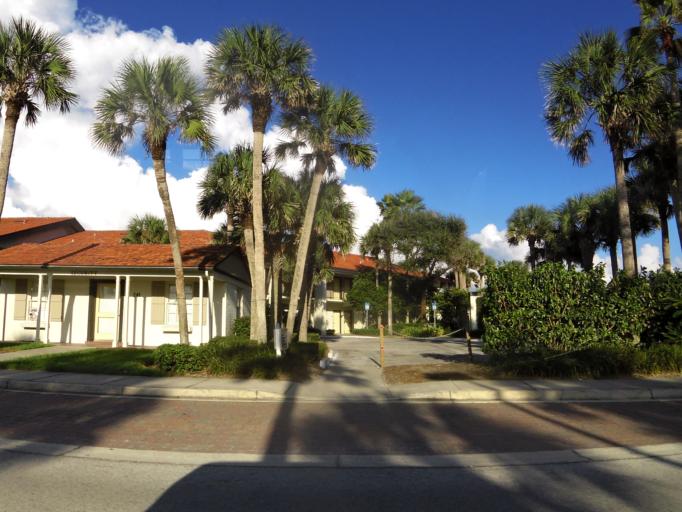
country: US
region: Florida
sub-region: Saint Johns County
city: Ponte Vedra Beach
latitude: 30.2407
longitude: -81.3783
